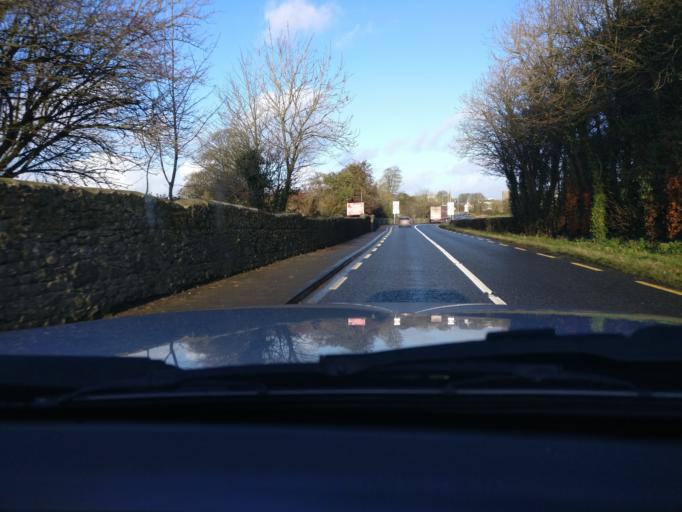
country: IE
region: Leinster
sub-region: An Iarmhi
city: Rathwire
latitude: 53.6067
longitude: -7.0993
